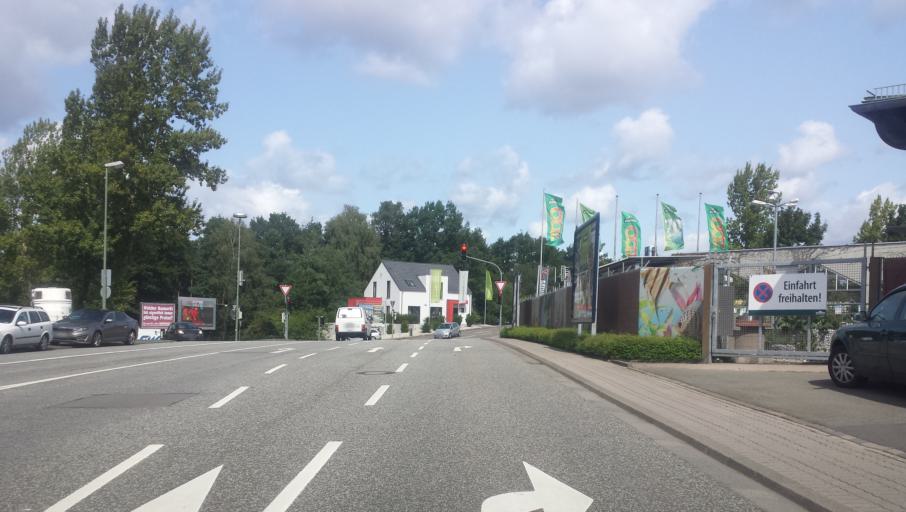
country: DE
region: Rheinland-Pfalz
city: Otterbach
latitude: 49.4407
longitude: 7.7112
